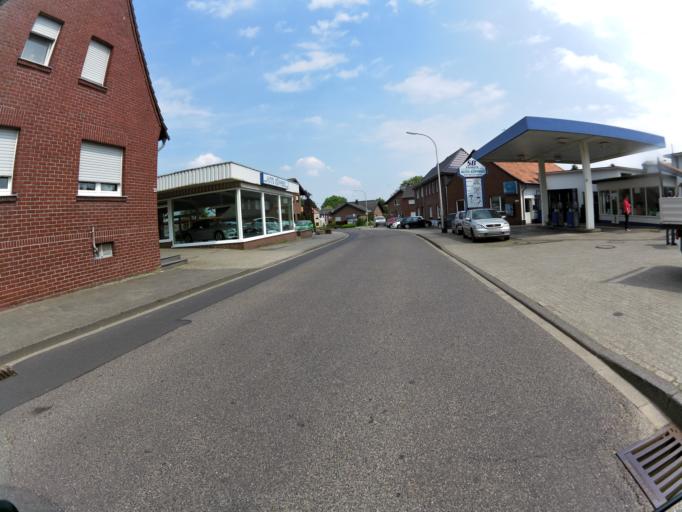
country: DE
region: North Rhine-Westphalia
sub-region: Regierungsbezirk Koln
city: Heinsberg
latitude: 51.0206
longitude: 6.1292
